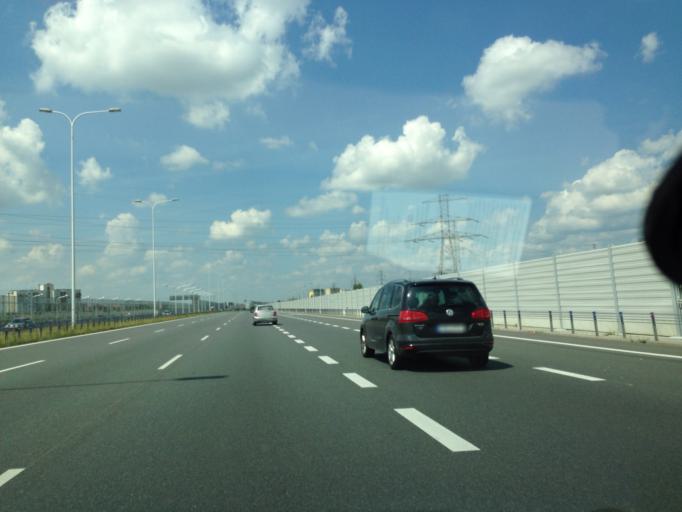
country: PL
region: Masovian Voivodeship
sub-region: Powiat pruszkowski
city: Michalowice
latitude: 52.1838
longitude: 20.8762
